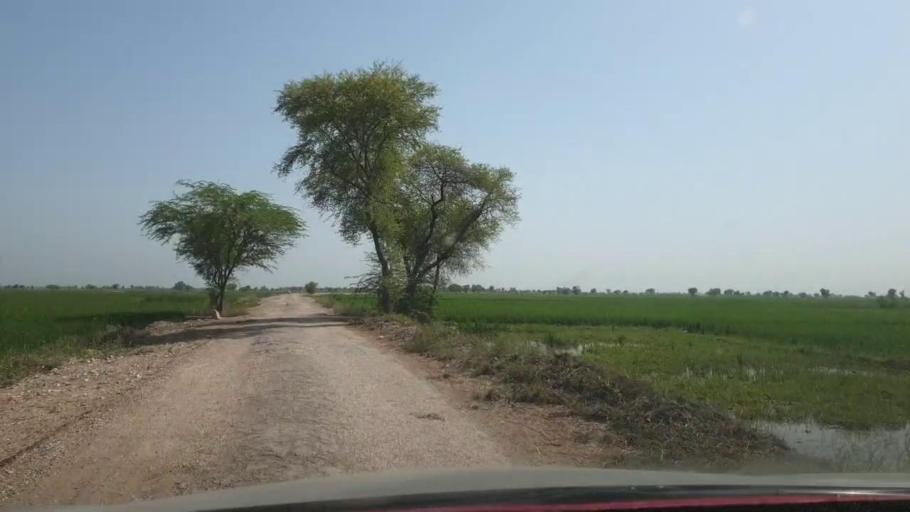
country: PK
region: Sindh
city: Nasirabad
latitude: 27.3698
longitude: 67.8529
